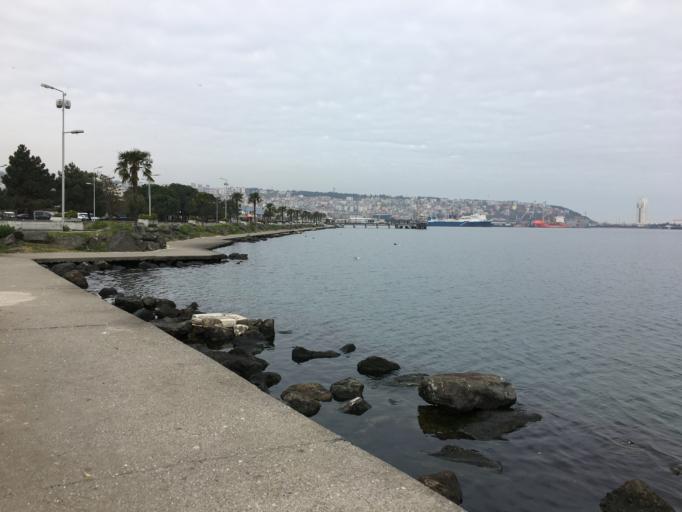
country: TR
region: Samsun
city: Samsun
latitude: 41.2906
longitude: 36.3422
